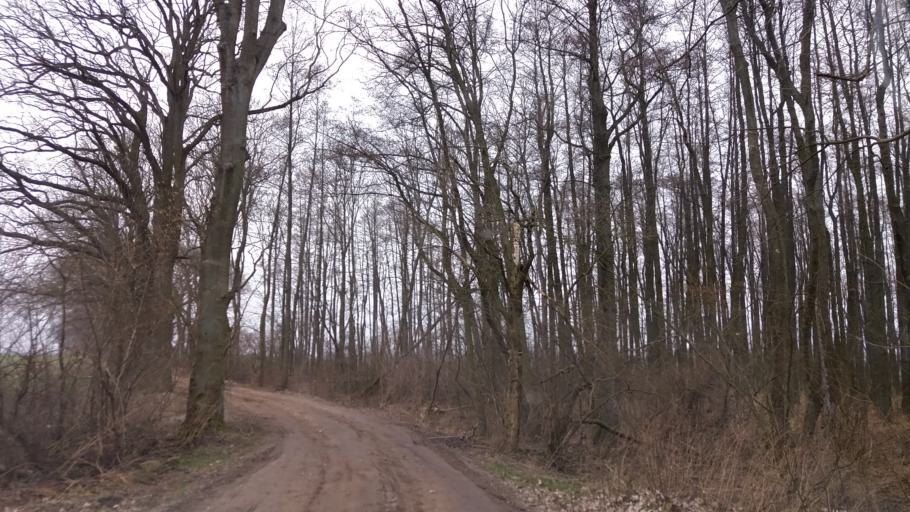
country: PL
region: West Pomeranian Voivodeship
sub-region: Powiat choszczenski
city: Choszczno
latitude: 53.1644
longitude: 15.3461
